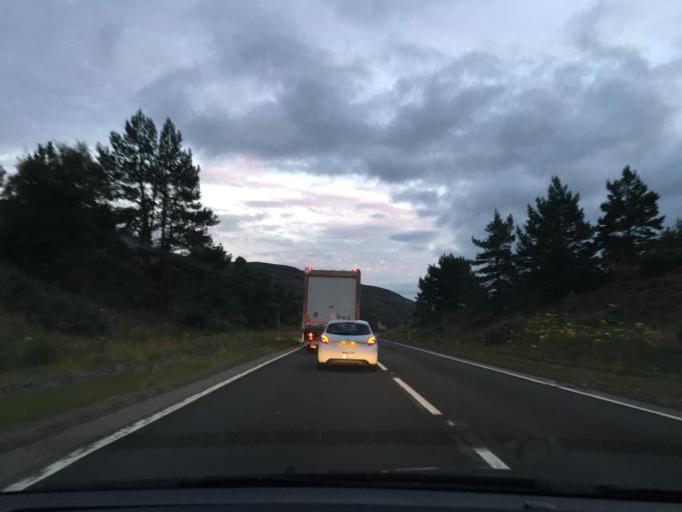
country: GB
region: Scotland
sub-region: Highland
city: Kingussie
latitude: 56.9864
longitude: -4.1774
